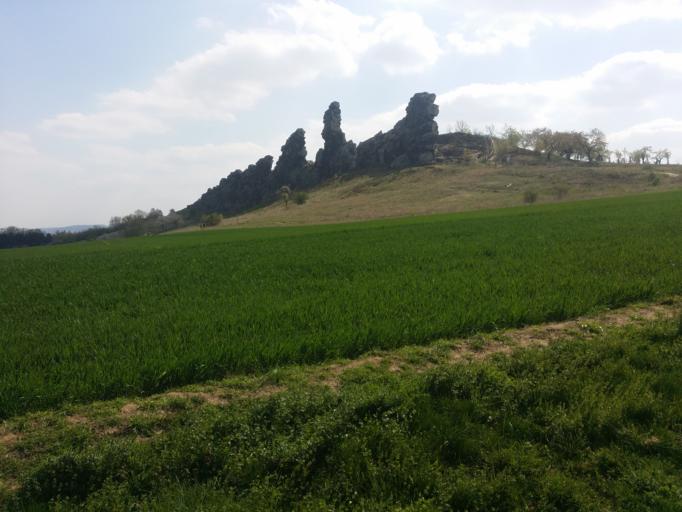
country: DE
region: Saxony-Anhalt
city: Weddersleben
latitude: 51.7597
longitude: 11.0803
